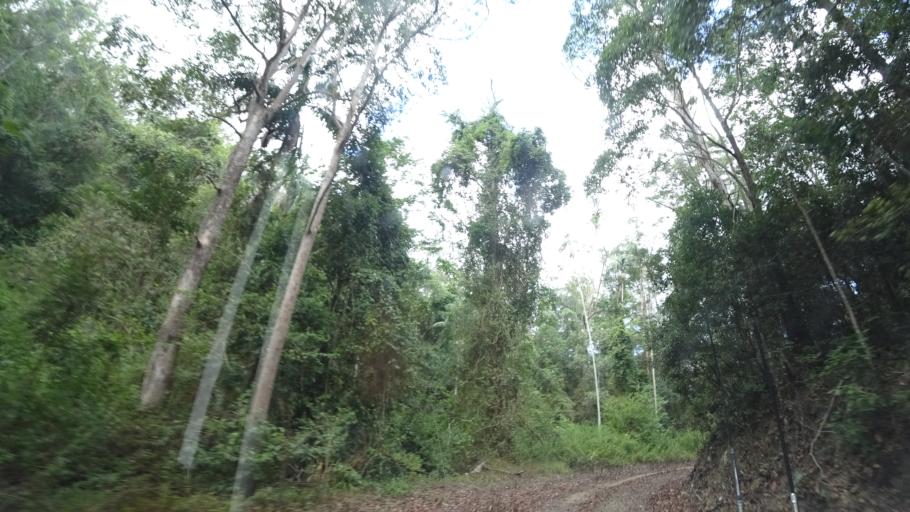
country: AU
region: Queensland
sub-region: Moreton Bay
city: Highvale
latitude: -27.3431
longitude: 152.7311
